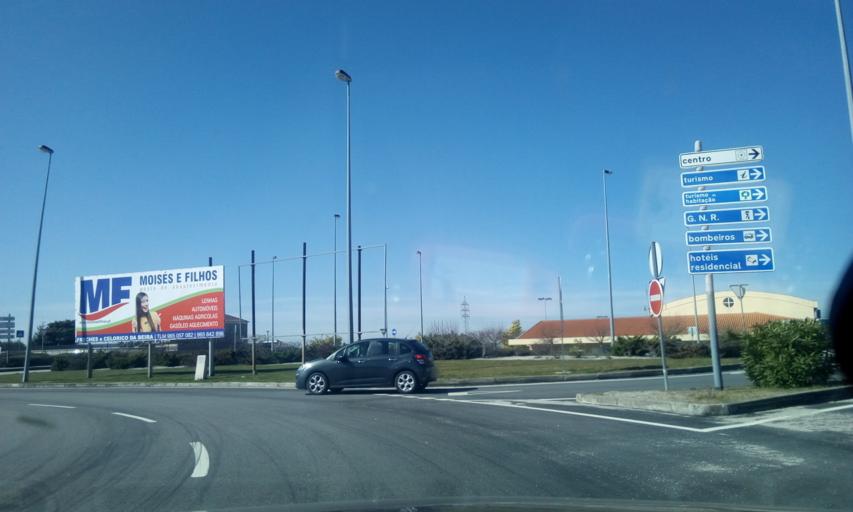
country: PT
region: Guarda
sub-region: Celorico da Beira
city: Celorico da Beira
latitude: 40.6266
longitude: -7.4013
